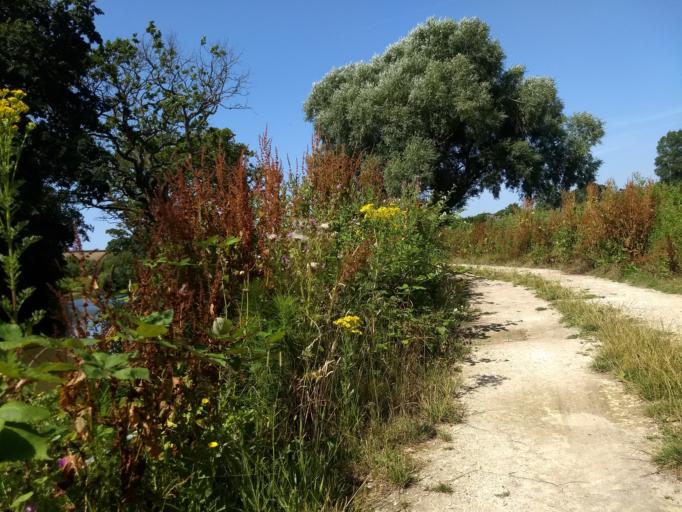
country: GB
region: England
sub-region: Isle of Wight
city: Newport
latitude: 50.6952
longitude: -1.3308
